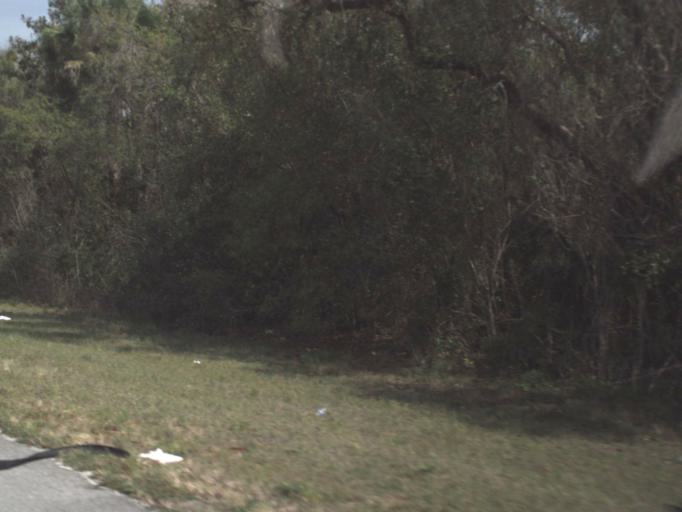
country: US
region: Florida
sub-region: Lake County
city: Astor
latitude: 29.1813
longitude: -81.6509
